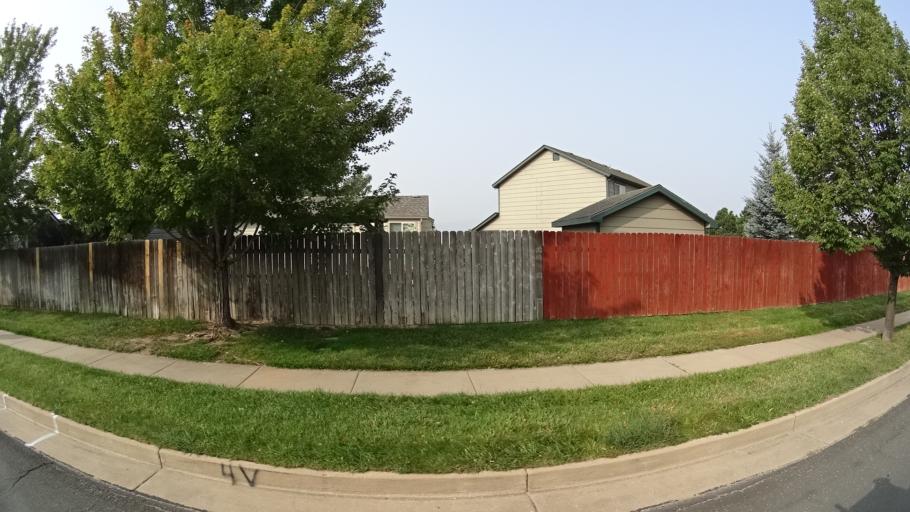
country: US
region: Colorado
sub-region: El Paso County
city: Black Forest
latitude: 38.9361
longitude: -104.7346
